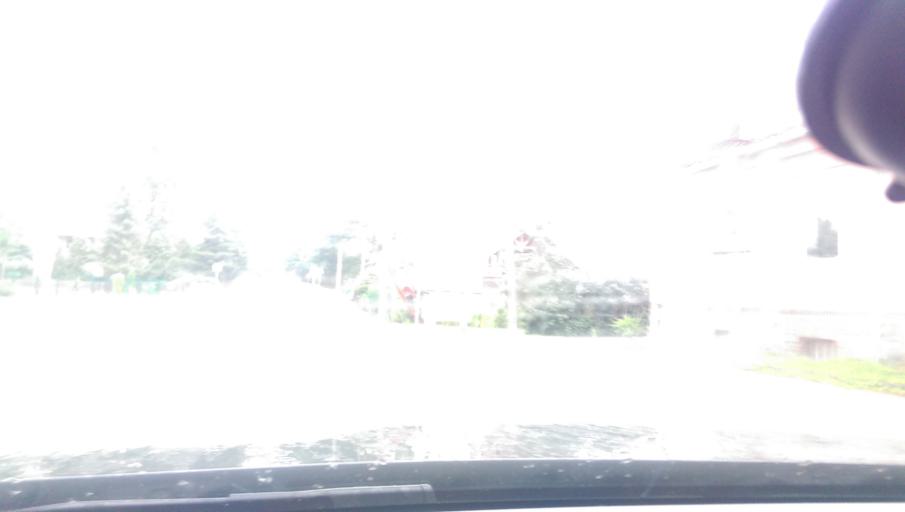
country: PL
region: Warmian-Masurian Voivodeship
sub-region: Powiat piski
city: Ruciane-Nida
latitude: 53.6880
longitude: 21.4908
